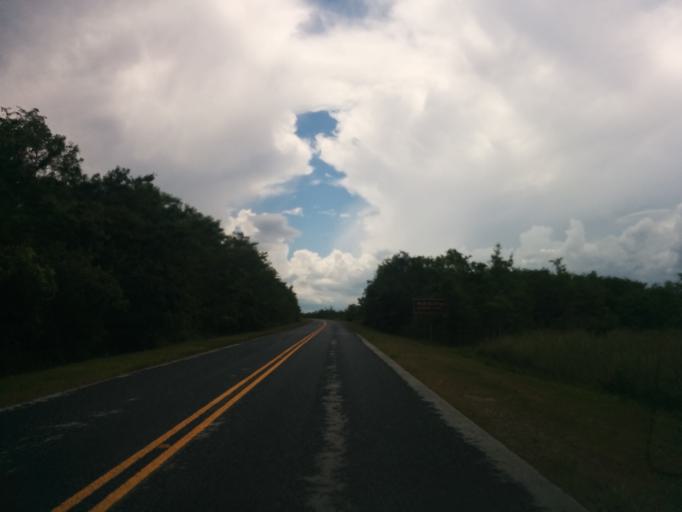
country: US
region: Florida
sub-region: Miami-Dade County
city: Florida City
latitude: 25.4334
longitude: -80.7481
